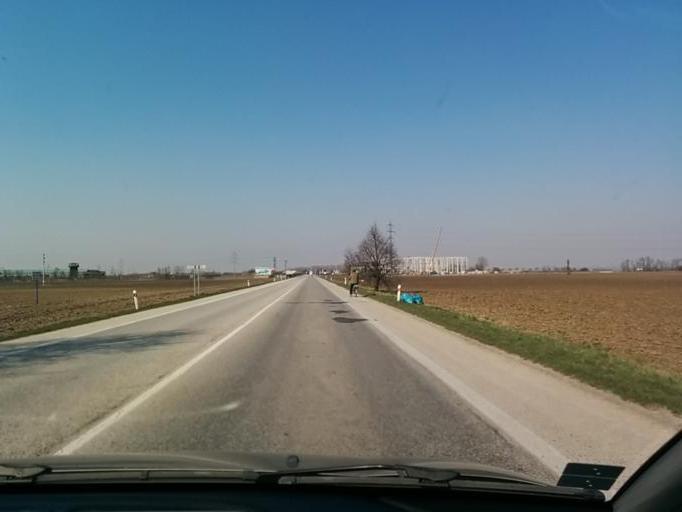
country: SK
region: Trnavsky
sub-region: Okres Galanta
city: Galanta
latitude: 48.2042
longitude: 17.7309
